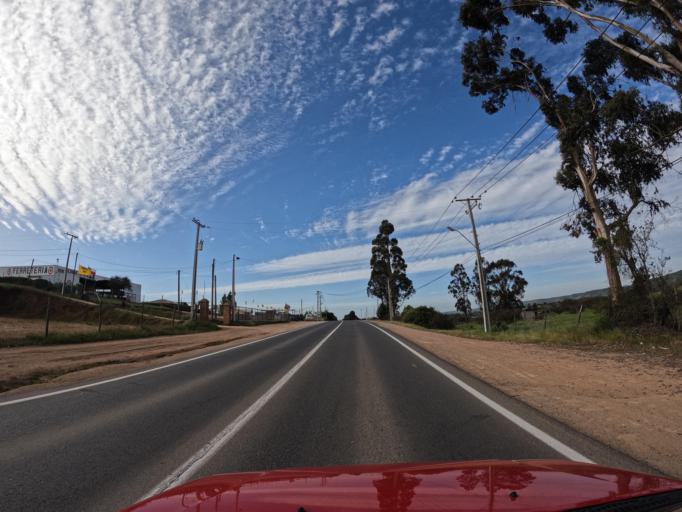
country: CL
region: Valparaiso
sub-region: San Antonio Province
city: San Antonio
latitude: -34.1348
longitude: -71.7284
